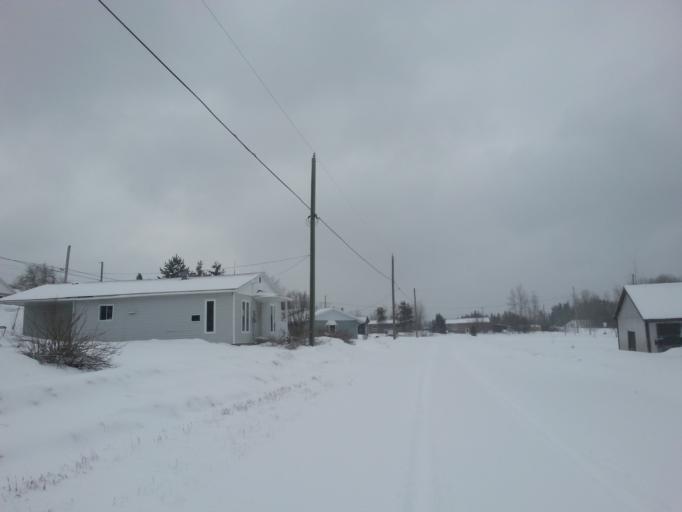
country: CA
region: Ontario
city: Kirkland Lake
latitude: 47.9365
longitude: -80.6509
